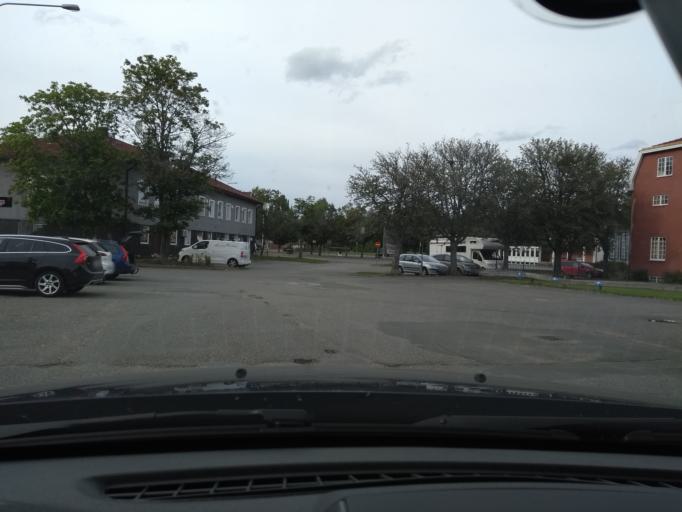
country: SE
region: Joenkoeping
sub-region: Eksjo Kommun
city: Mariannelund
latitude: 57.6161
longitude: 15.5727
